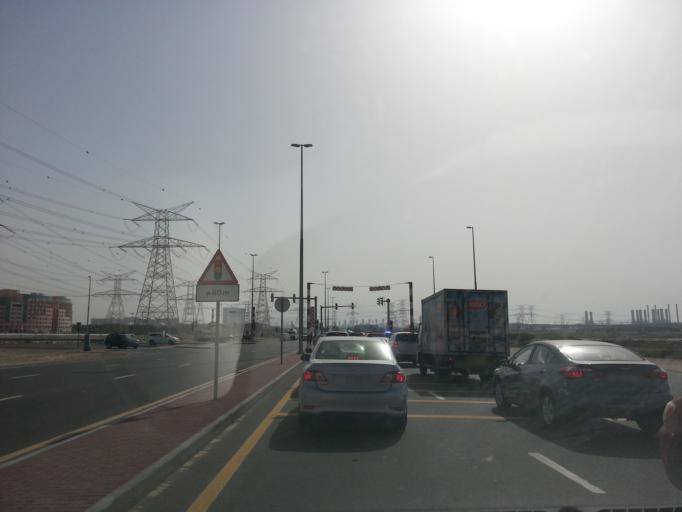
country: AE
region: Dubai
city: Dubai
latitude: 25.0529
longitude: 55.1332
